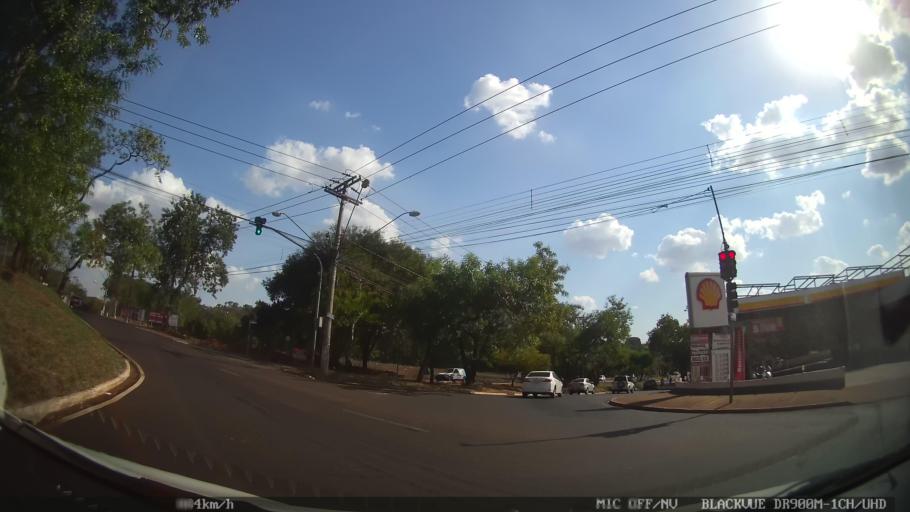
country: BR
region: Sao Paulo
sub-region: Ribeirao Preto
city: Ribeirao Preto
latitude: -21.2036
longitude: -47.8270
